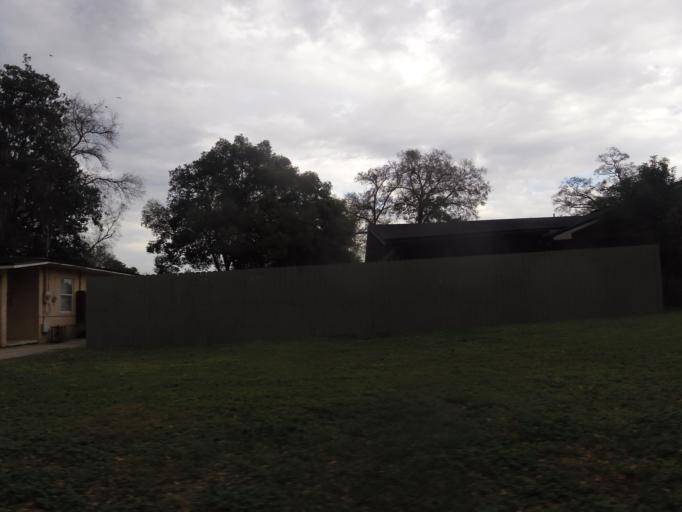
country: US
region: Florida
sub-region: Duval County
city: Jacksonville
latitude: 30.3405
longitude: -81.6065
